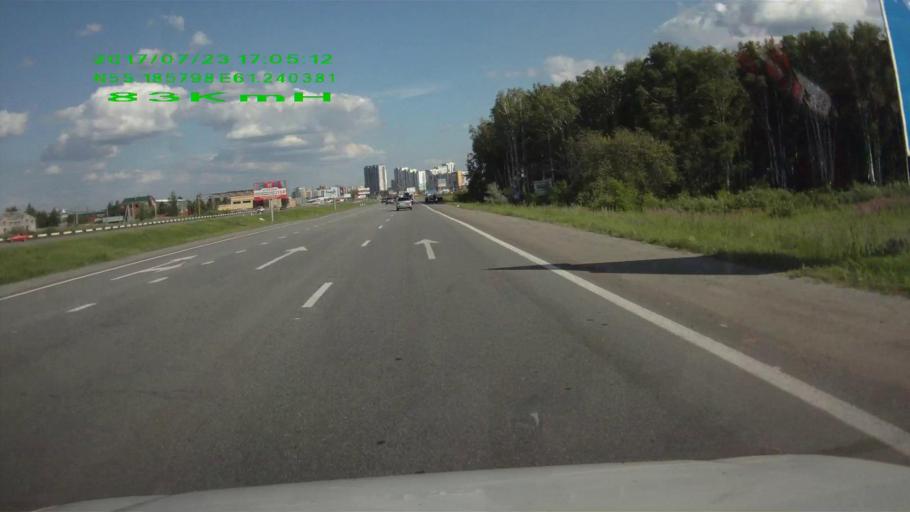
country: RU
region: Chelyabinsk
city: Roshchino
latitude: 55.1852
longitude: 61.2414
